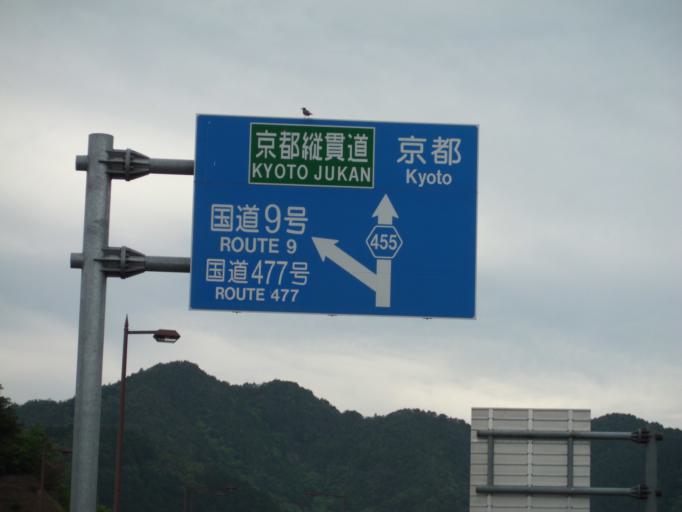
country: JP
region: Kyoto
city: Kameoka
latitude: 35.0751
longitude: 135.5272
